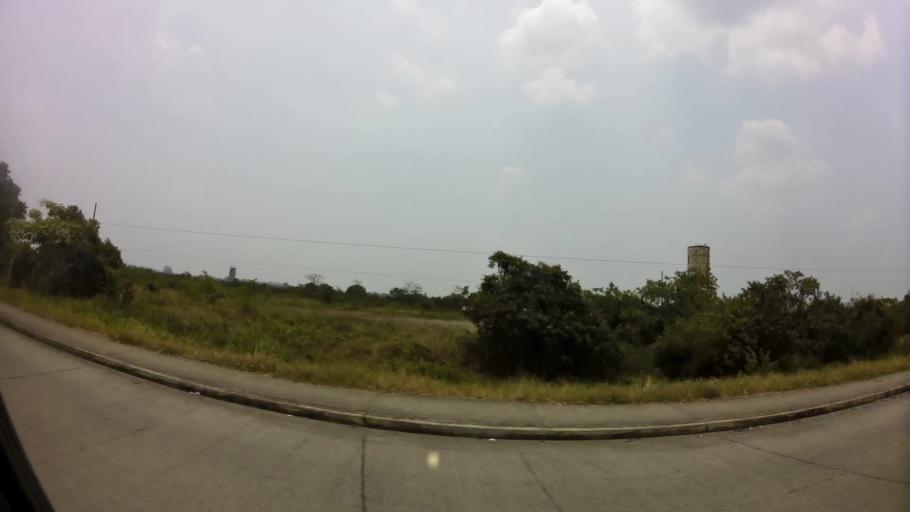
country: HN
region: Cortes
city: La Lima
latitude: 15.4519
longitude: -87.9347
